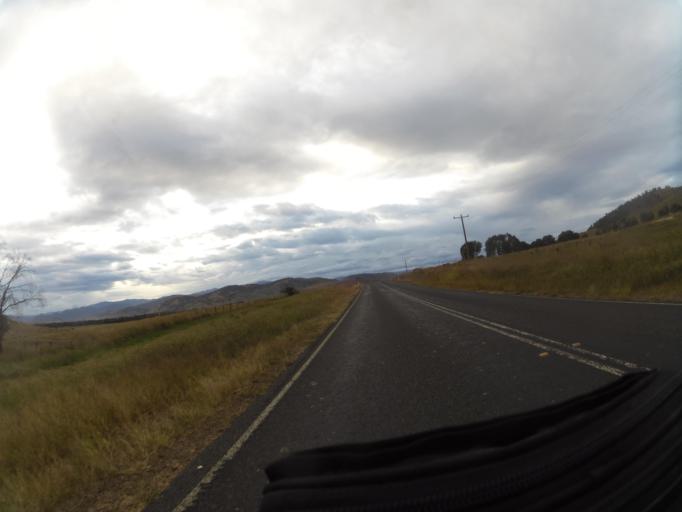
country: AU
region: New South Wales
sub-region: Greater Hume Shire
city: Holbrook
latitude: -36.0734
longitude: 147.9671
